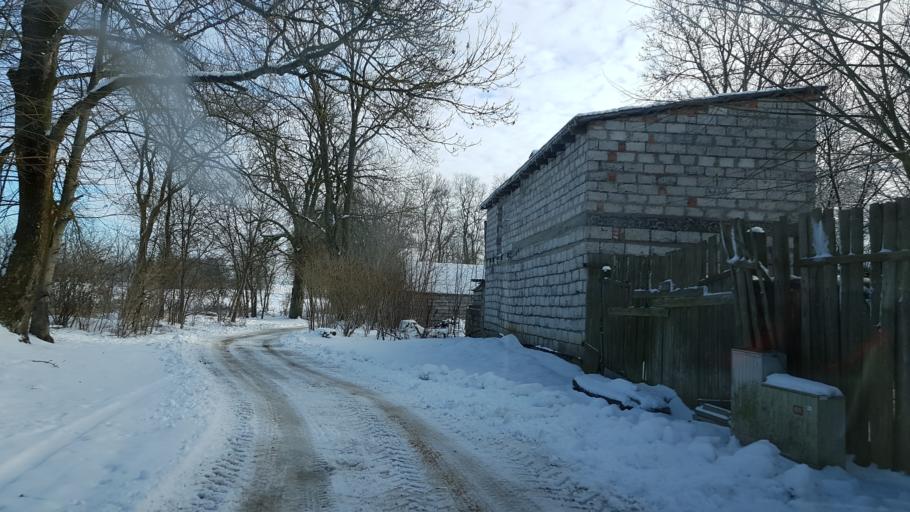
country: PL
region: West Pomeranian Voivodeship
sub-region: Powiat drawski
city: Drawsko Pomorskie
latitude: 53.5358
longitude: 15.7728
